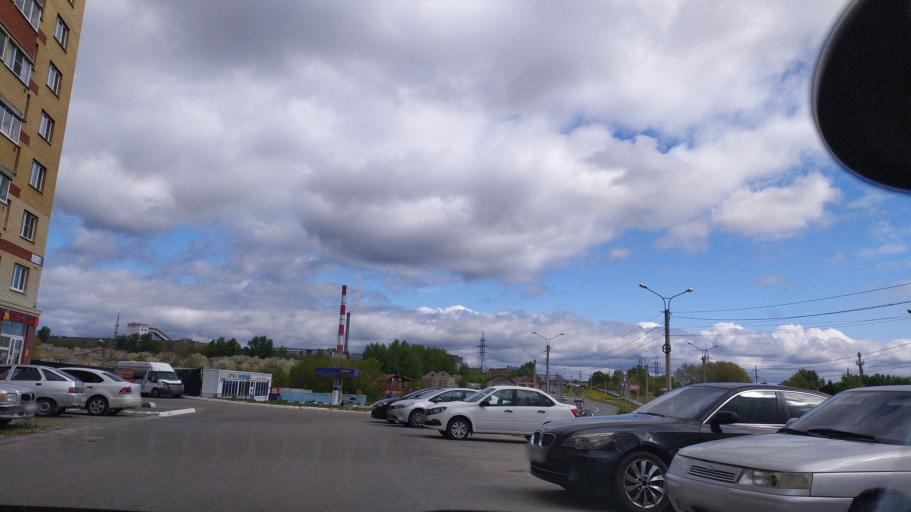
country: RU
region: Chuvashia
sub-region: Cheboksarskiy Rayon
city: Cheboksary
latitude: 56.1089
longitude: 47.2930
